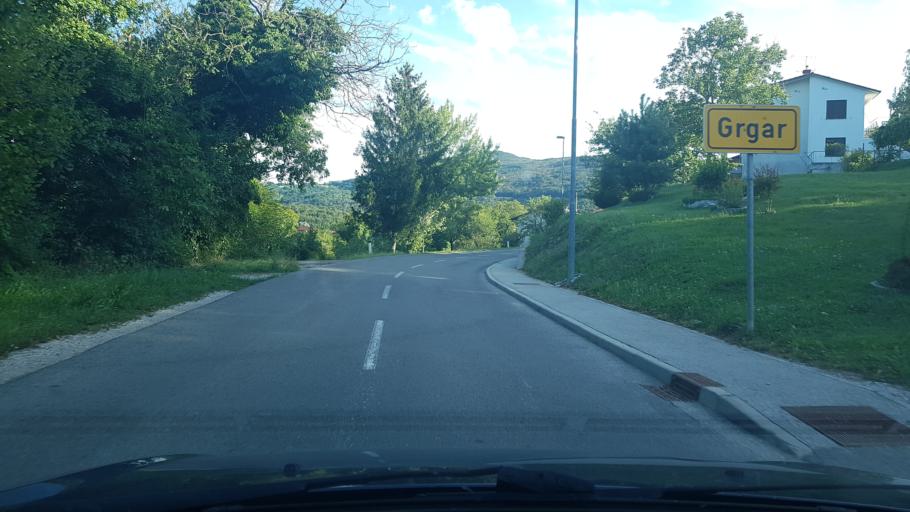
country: SI
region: Nova Gorica
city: Solkan
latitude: 46.0036
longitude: 13.6729
